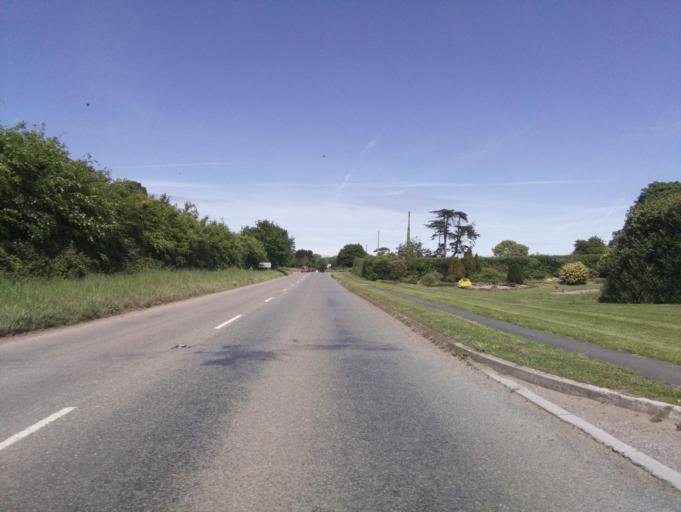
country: GB
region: England
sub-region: Devon
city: Budleigh Salterton
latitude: 50.6457
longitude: -3.3172
